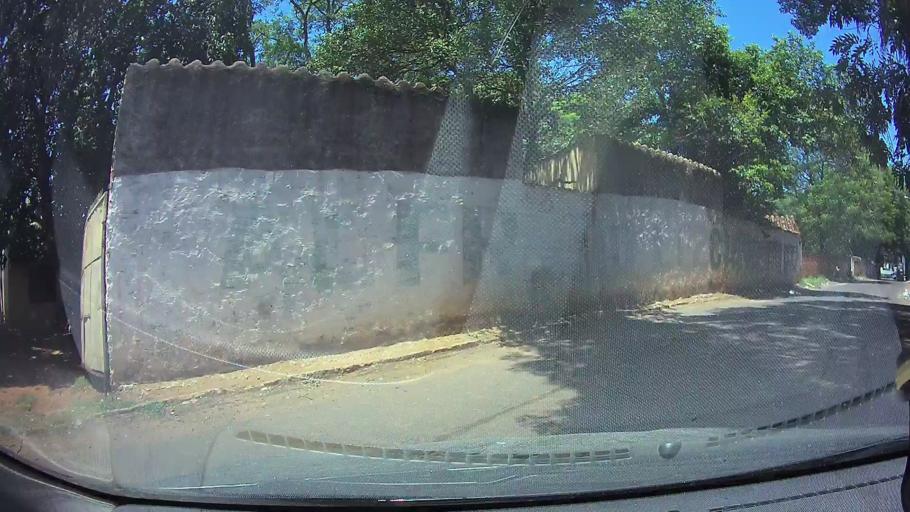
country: PY
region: Central
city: San Lorenzo
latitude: -25.3532
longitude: -57.4887
